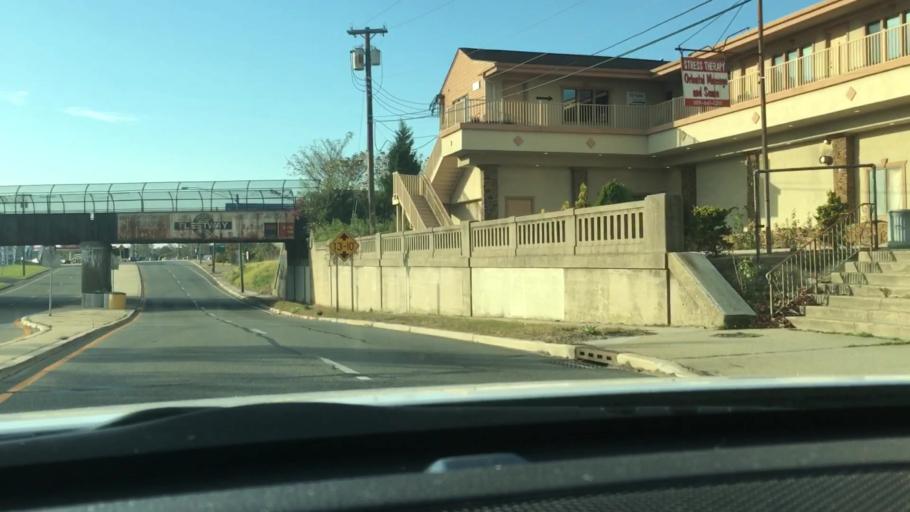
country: US
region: New Jersey
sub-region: Atlantic County
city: Pleasantville
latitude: 39.3910
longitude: -74.5264
